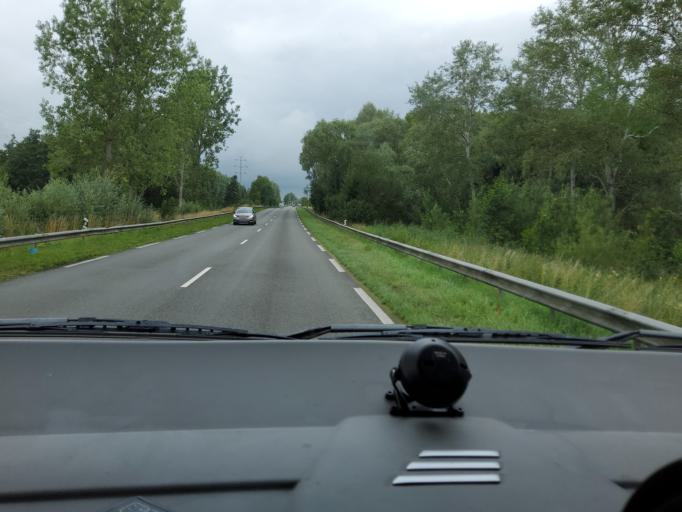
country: FR
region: Nord-Pas-de-Calais
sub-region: Departement du Pas-de-Calais
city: Serques
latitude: 50.8152
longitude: 2.1939
